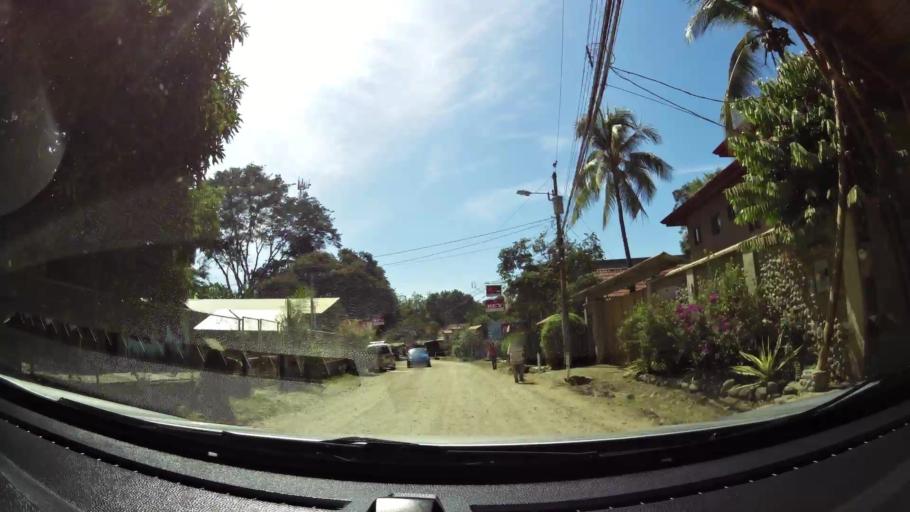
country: CR
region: San Jose
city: San Isidro
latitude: 9.2542
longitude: -83.8639
